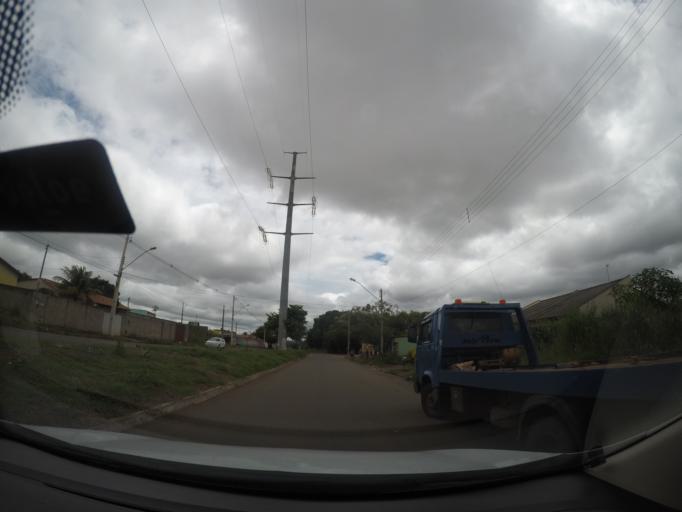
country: BR
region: Goias
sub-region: Goiania
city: Goiania
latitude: -16.7294
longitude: -49.3583
